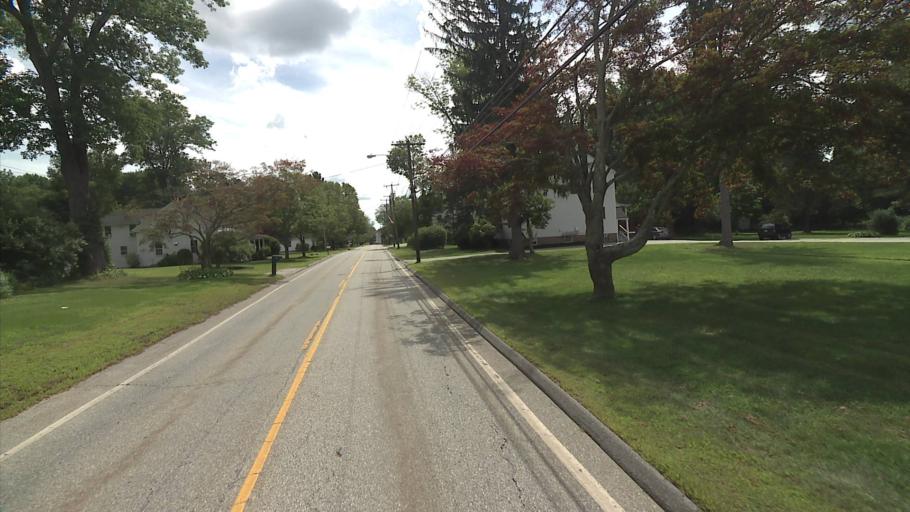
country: US
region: Connecticut
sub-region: Windham County
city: Thompson
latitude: 41.9607
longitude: -71.8655
